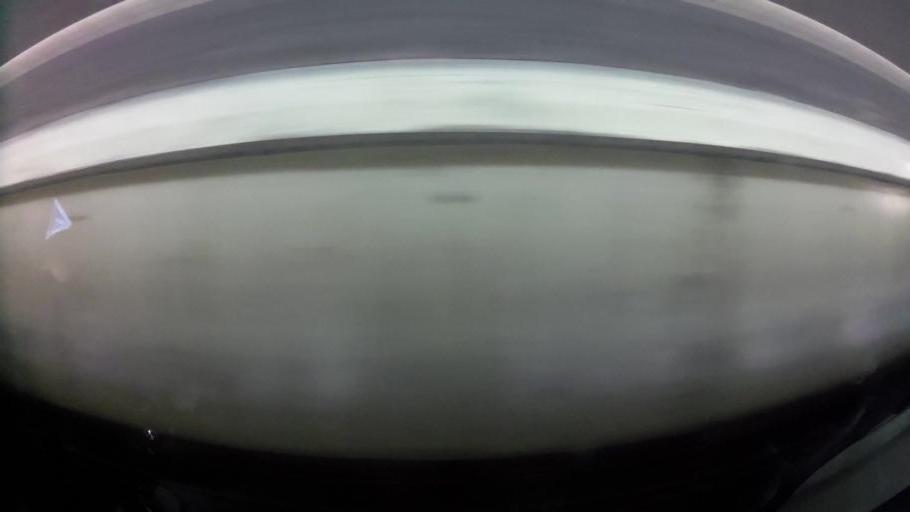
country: SG
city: Singapore
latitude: 1.2947
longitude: 103.8417
